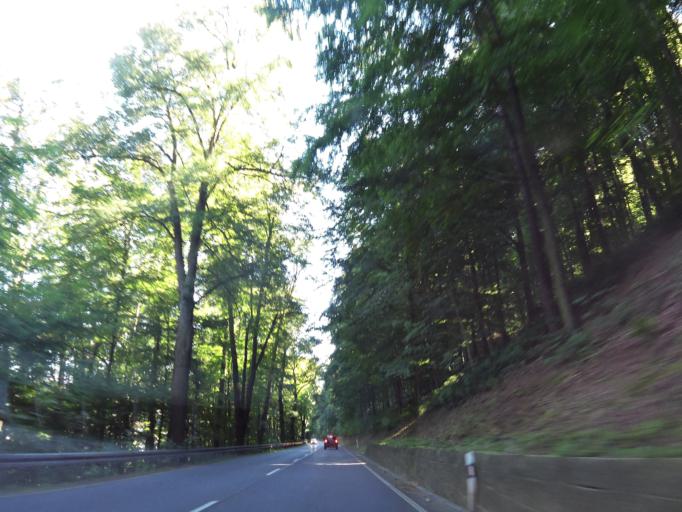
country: DE
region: Saxony
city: Konigstein
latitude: 50.9233
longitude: 14.0574
